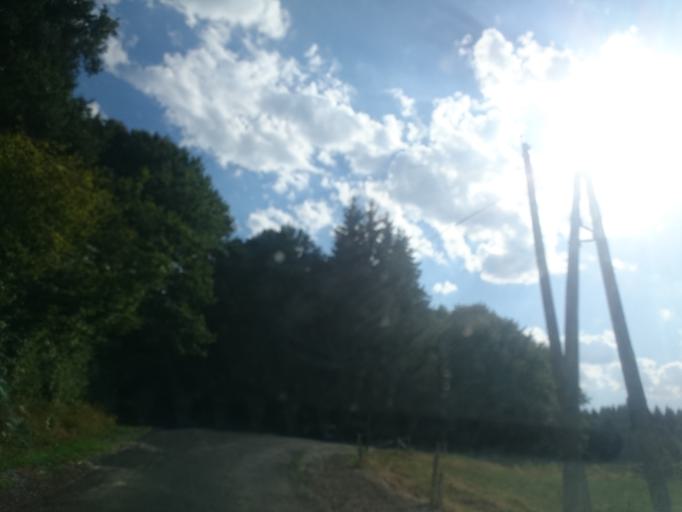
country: FR
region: Auvergne
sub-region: Departement du Cantal
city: Laroquebrou
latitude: 44.8949
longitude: 2.1708
